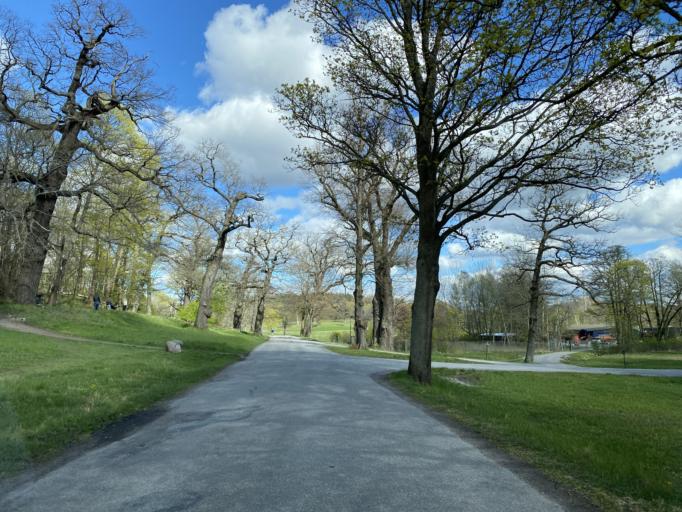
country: SE
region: Stockholm
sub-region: Stockholms Kommun
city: OEstermalm
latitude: 59.3626
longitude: 18.0798
